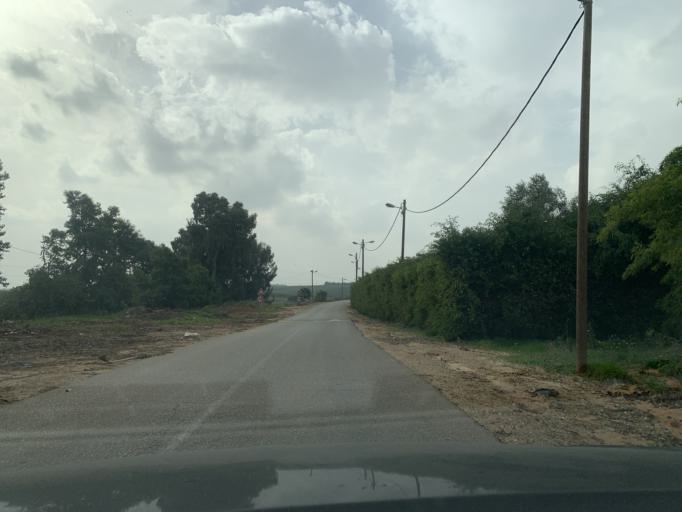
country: IL
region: Central District
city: Tirah
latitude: 32.2149
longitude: 34.9409
